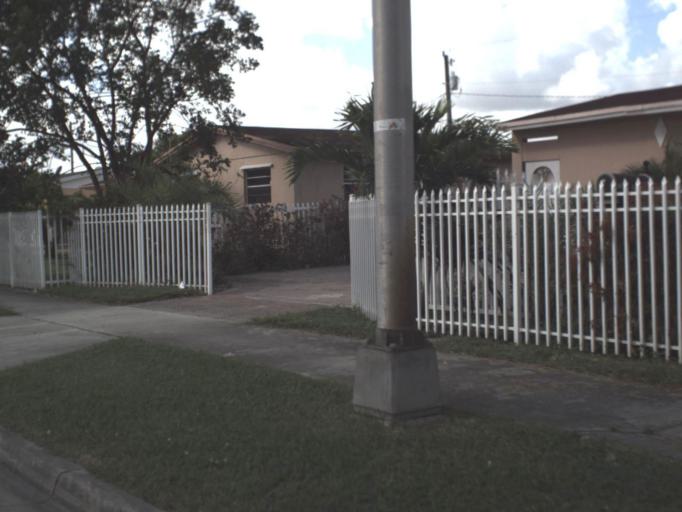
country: US
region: Florida
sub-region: Miami-Dade County
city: Leisure City
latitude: 25.4996
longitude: -80.4231
